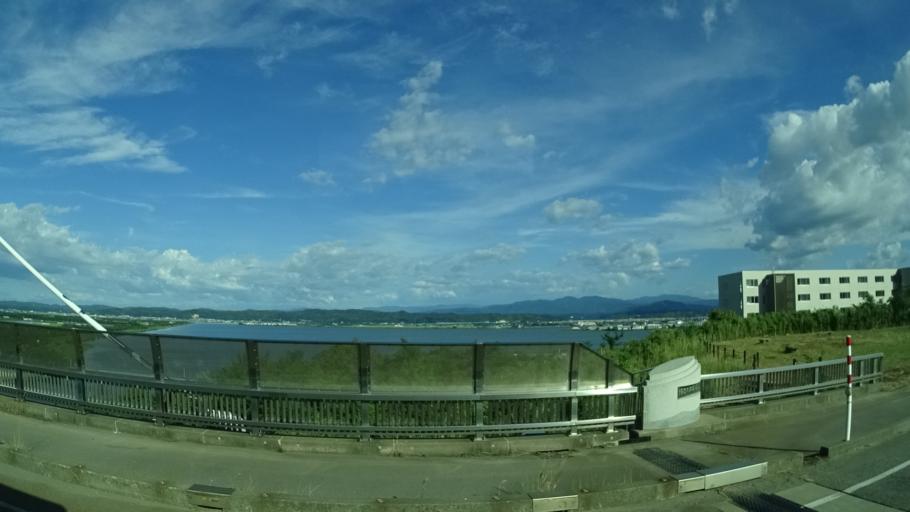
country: JP
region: Ishikawa
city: Kanazawa-shi
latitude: 36.6591
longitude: 136.6498
